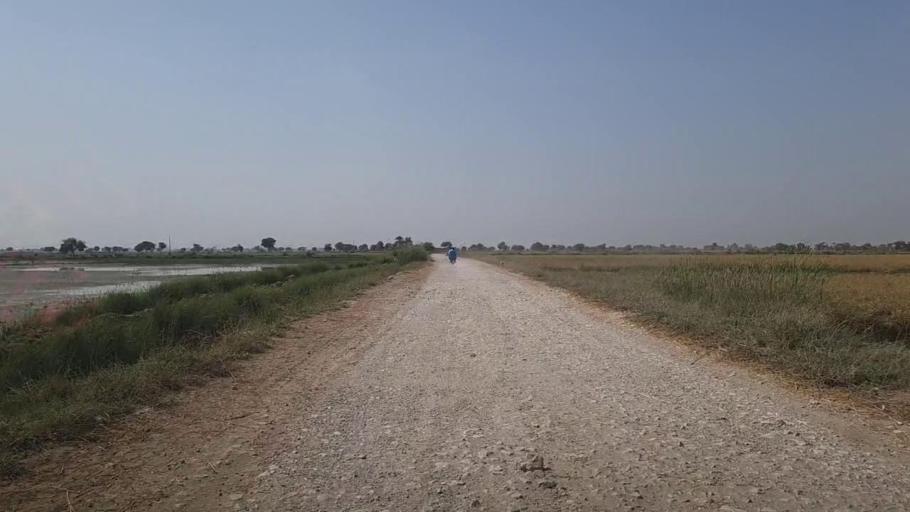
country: PK
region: Sindh
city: Kandhkot
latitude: 28.3925
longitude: 69.3079
